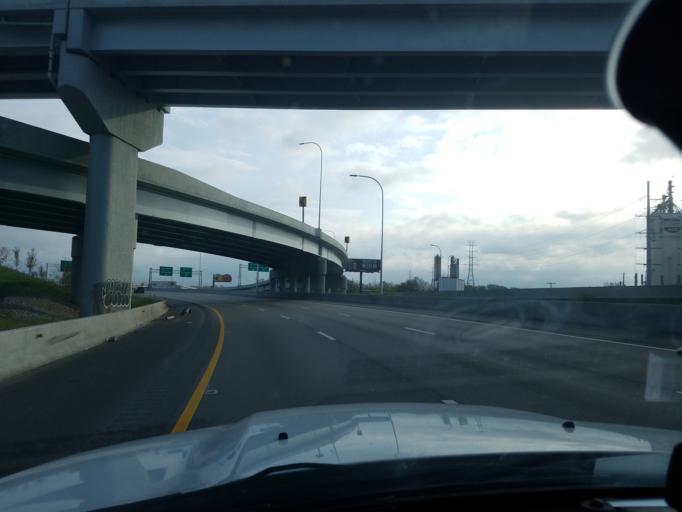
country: US
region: Kentucky
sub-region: Jefferson County
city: Louisville
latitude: 38.2580
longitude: -85.7408
